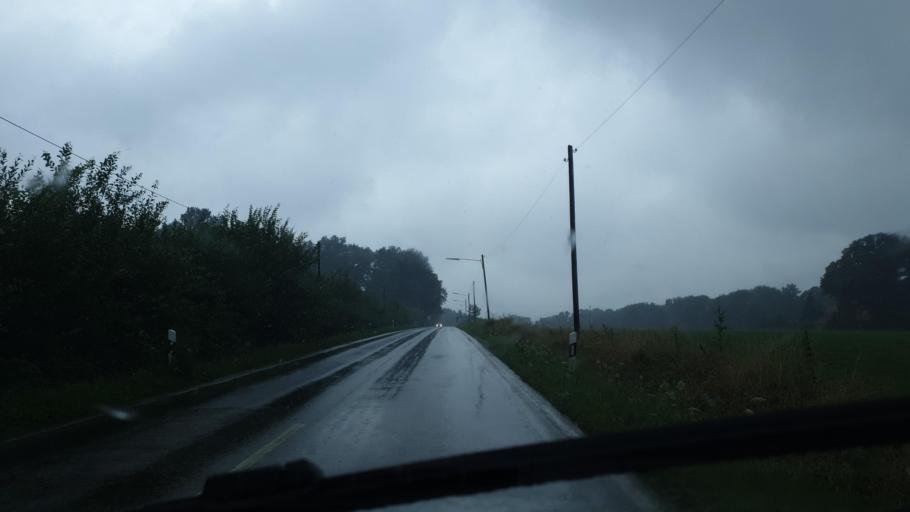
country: DE
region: North Rhine-Westphalia
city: Loehne
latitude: 52.1745
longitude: 8.6857
